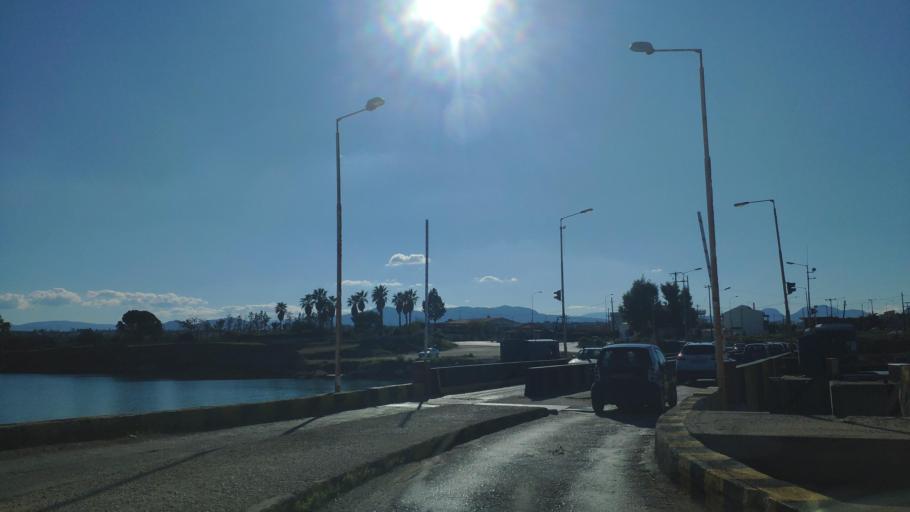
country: GR
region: Peloponnese
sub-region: Nomos Korinthias
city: Korinthos
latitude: 37.9505
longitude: 22.9627
